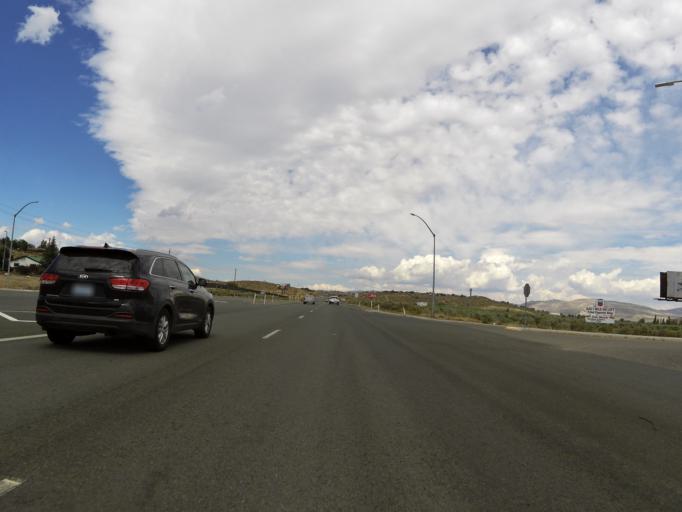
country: US
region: Nevada
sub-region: Douglas County
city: Indian Hills
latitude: 39.0738
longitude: -119.7793
